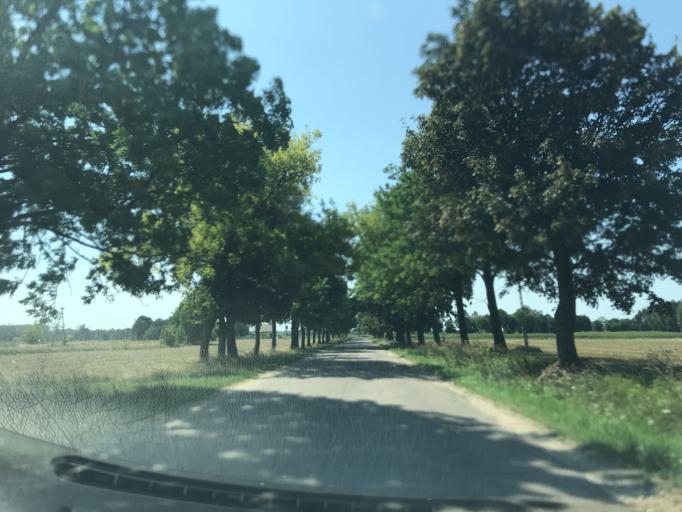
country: PL
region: Kujawsko-Pomorskie
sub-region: Powiat lipnowski
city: Chrostkowo
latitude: 52.9879
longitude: 19.2727
